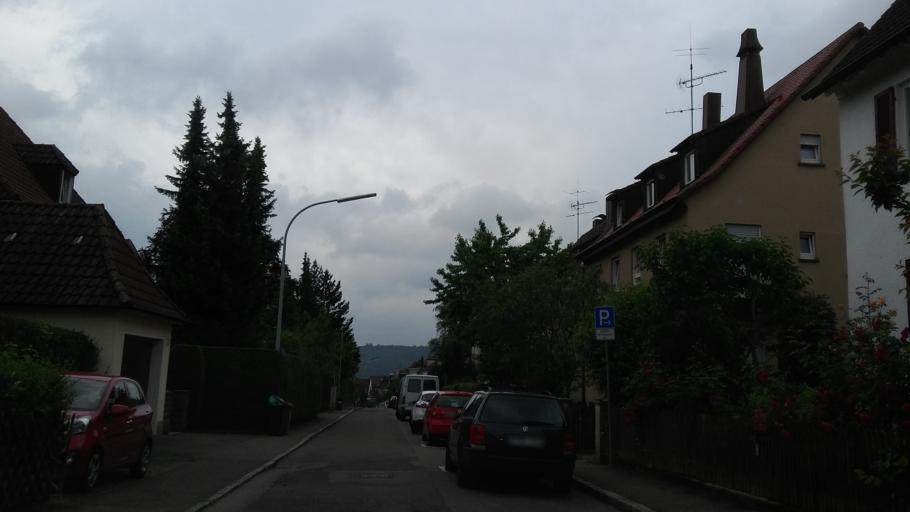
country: DE
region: Baden-Wuerttemberg
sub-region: Regierungsbezirk Stuttgart
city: Esslingen
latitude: 48.7372
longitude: 9.3295
